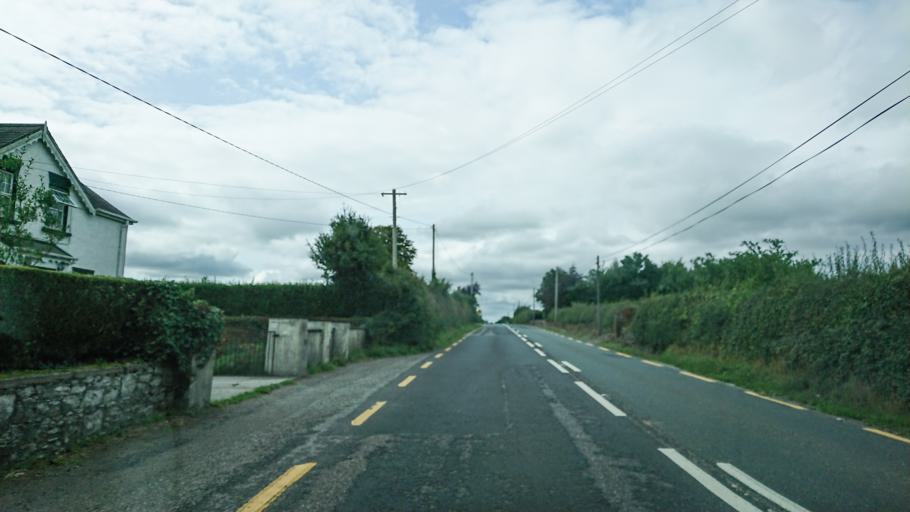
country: IE
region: Munster
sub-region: Waterford
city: Dungarvan
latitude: 52.1149
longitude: -7.7156
